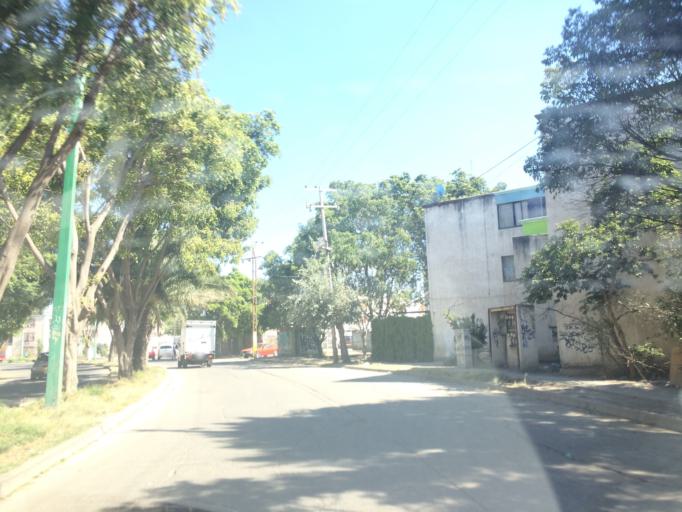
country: MX
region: Guanajuato
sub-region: Leon
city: San Jose de Duran (Los Troncoso)
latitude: 21.0963
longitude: -101.6704
